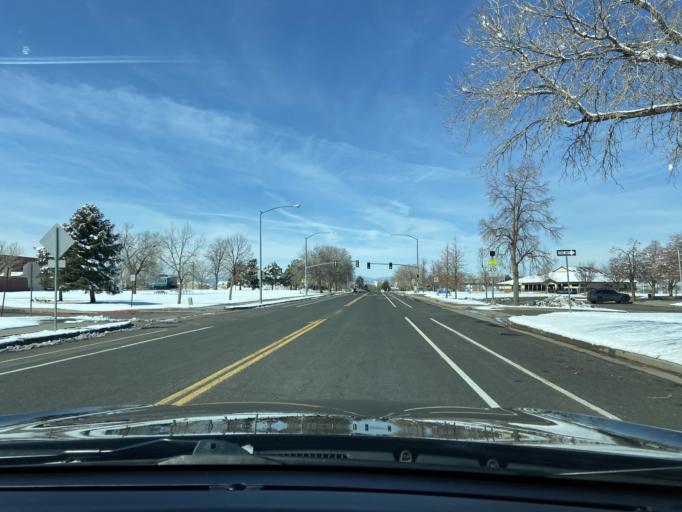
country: US
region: Colorado
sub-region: Adams County
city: Aurora
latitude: 39.7039
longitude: -104.8578
